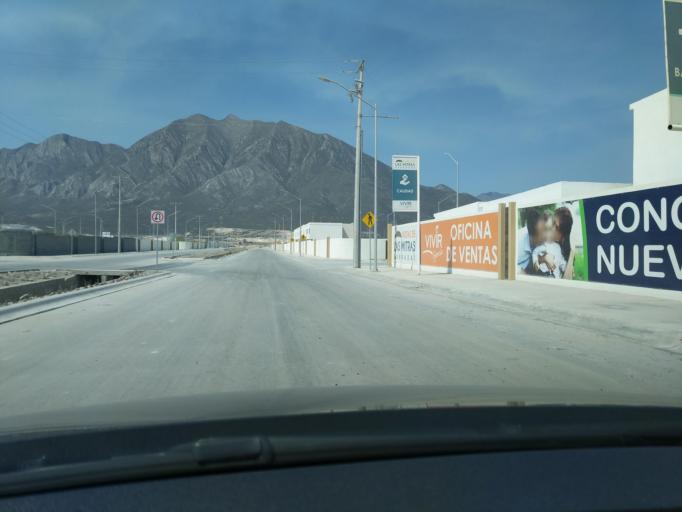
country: MX
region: Nuevo Leon
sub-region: Garcia
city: Valle de Lincoln
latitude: 25.7942
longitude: -100.4709
